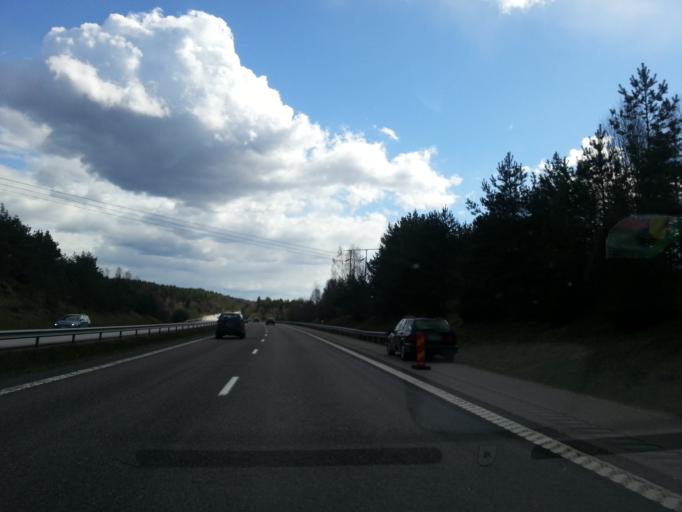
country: SE
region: Vaestra Goetaland
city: Svanesund
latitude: 58.1068
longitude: 11.8789
